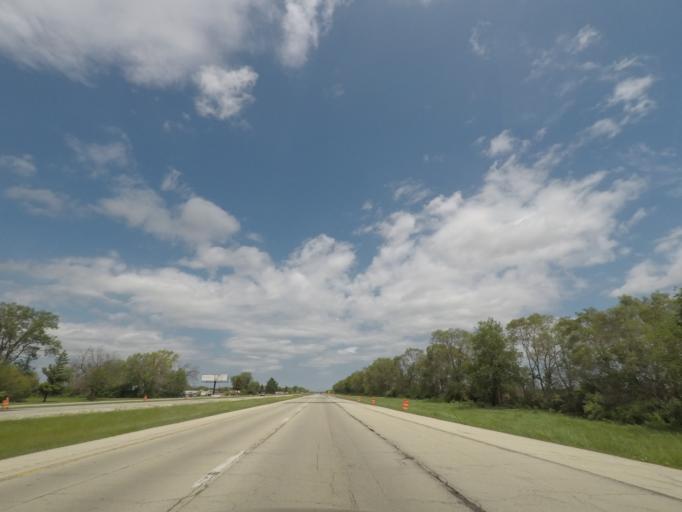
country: US
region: Illinois
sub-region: Winnebago County
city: South Beloit
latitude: 42.4644
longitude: -89.0193
